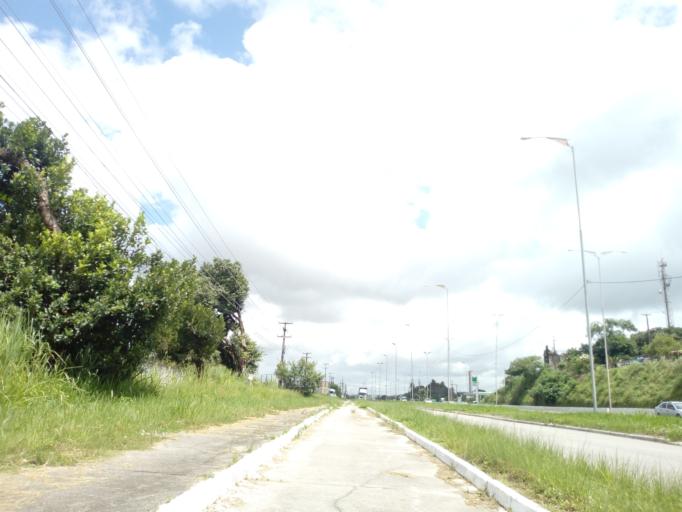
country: BR
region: Pernambuco
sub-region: Cabo De Santo Agostinho
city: Cabo
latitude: -8.2702
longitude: -35.0223
